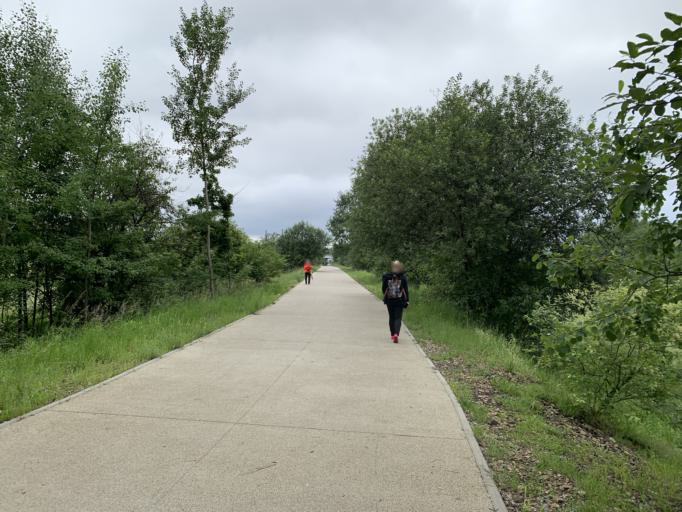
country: PL
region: Silesian Voivodeship
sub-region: Bytom
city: Bytom
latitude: 50.3324
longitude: 18.9518
